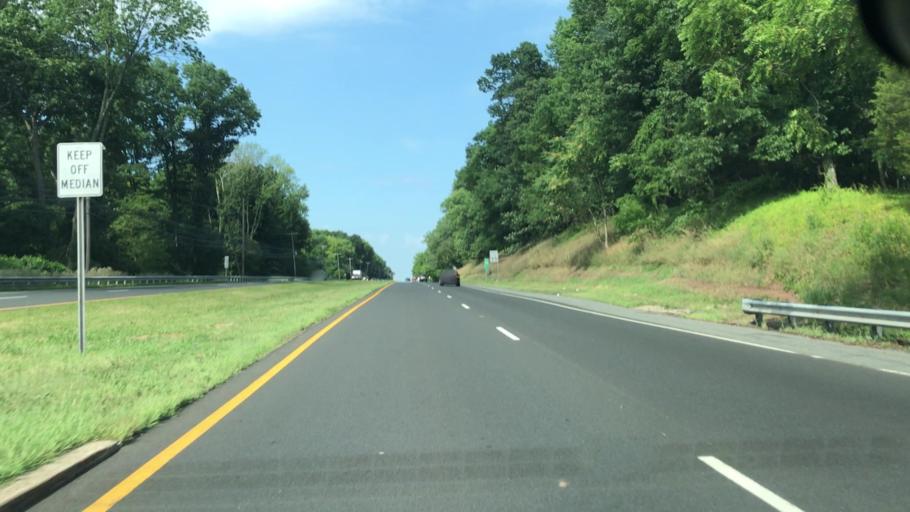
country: US
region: New Jersey
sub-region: Hunterdon County
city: Whitehouse Station
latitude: 40.5406
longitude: -74.7589
